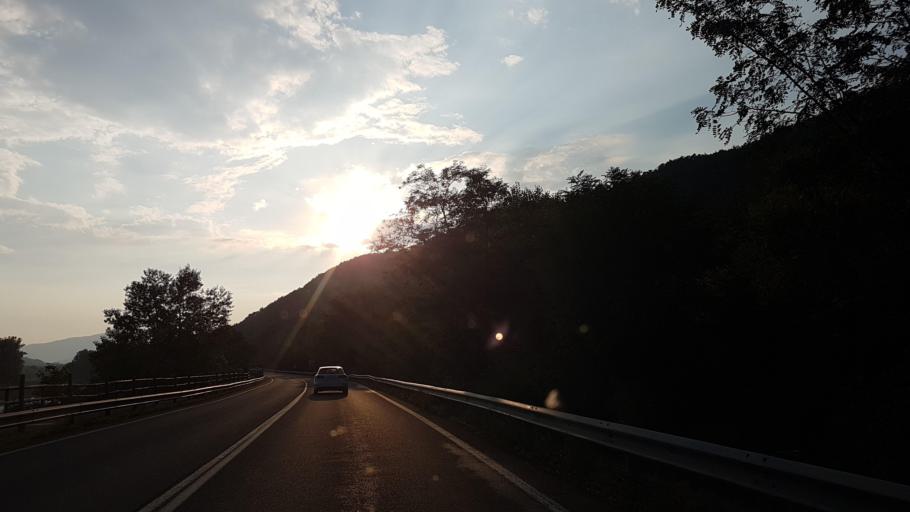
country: IT
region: Emilia-Romagna
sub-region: Provincia di Parma
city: Borgo Val di Taro
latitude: 44.5010
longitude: 9.8104
